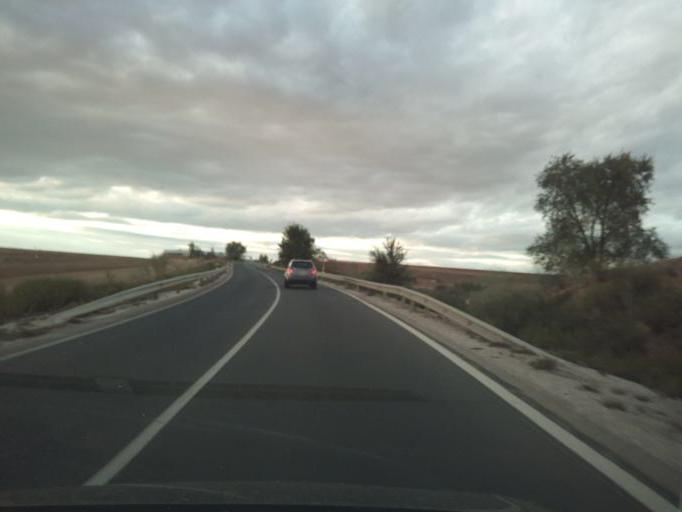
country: ES
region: Madrid
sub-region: Provincia de Madrid
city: Ajalvir
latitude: 40.5274
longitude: -3.4914
